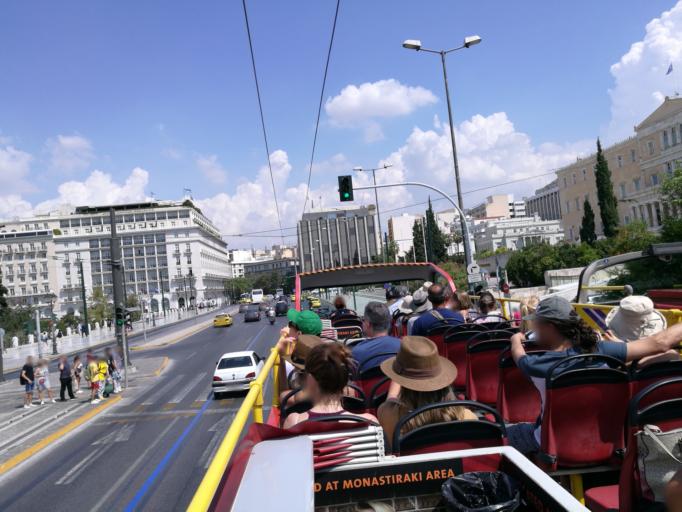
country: GR
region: Attica
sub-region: Nomarchia Athinas
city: Athens
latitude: 37.9746
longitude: 23.7356
